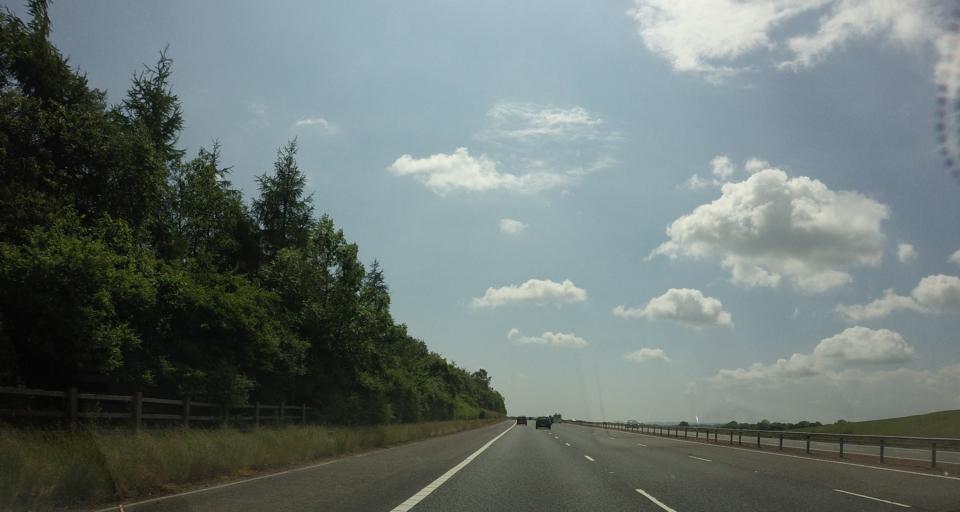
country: GB
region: Scotland
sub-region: Dumfries and Galloway
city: Lochmaben
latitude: 55.2043
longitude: -3.4120
